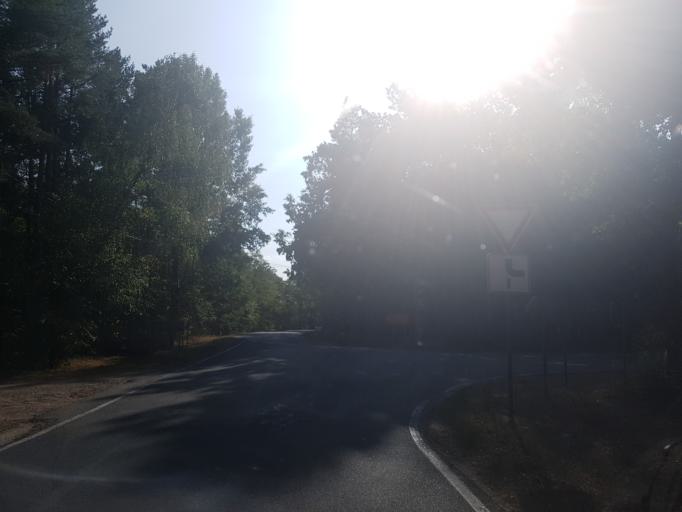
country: DE
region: Saxony-Anhalt
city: Jessen
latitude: 51.8662
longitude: 13.0286
